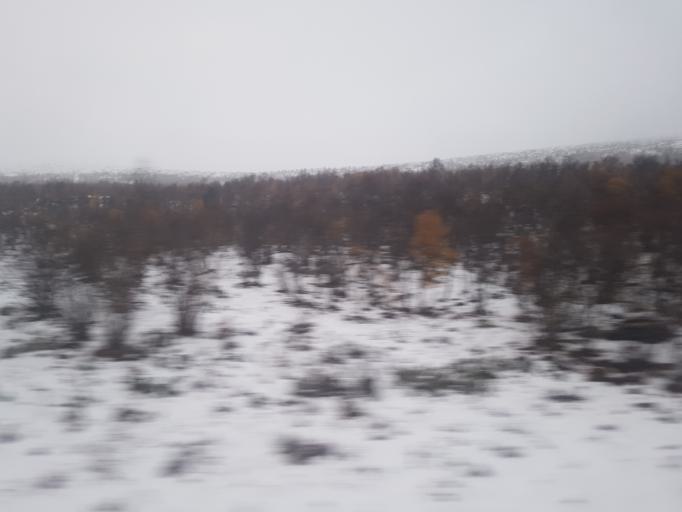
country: NO
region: Oppland
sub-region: Dovre
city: Dovre
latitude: 62.1754
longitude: 9.4491
